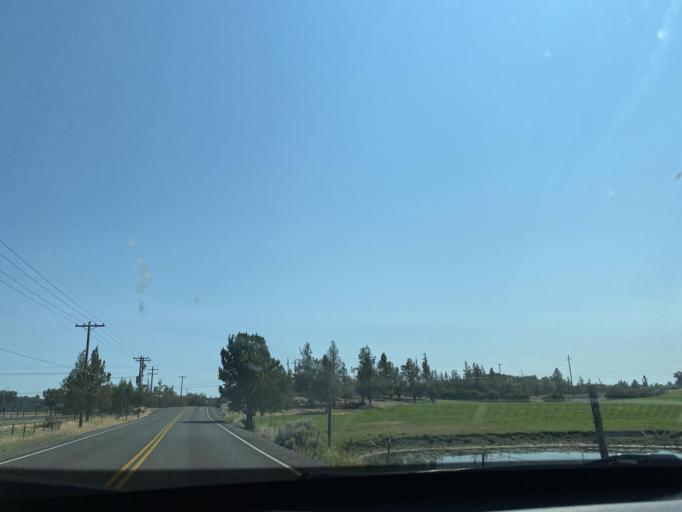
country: US
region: Oregon
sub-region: Deschutes County
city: Terrebonne
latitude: 44.3578
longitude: -121.1587
